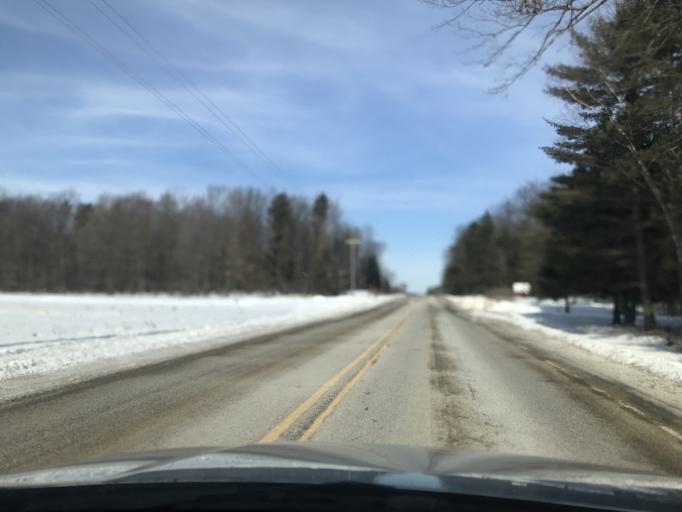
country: US
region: Wisconsin
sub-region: Oconto County
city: Oconto Falls
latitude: 45.1367
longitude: -88.1774
